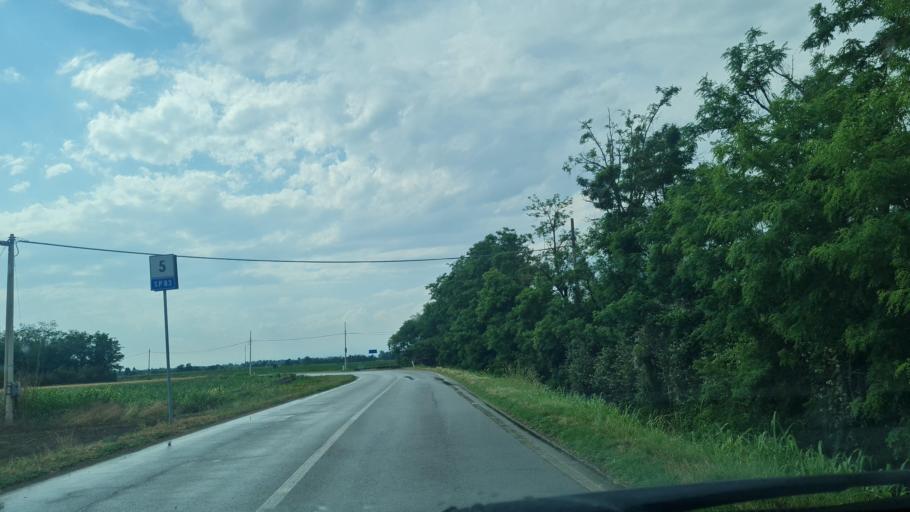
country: IT
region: Piedmont
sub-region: Provincia di Novara
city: Cameri
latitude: 45.5054
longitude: 8.6448
